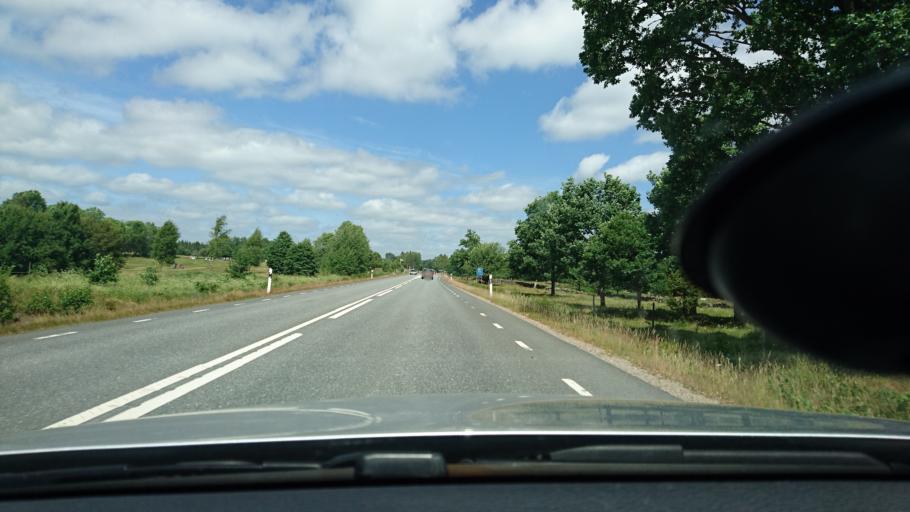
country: SE
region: Kronoberg
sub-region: Alvesta Kommun
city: Moheda
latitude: 56.9612
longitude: 14.5724
